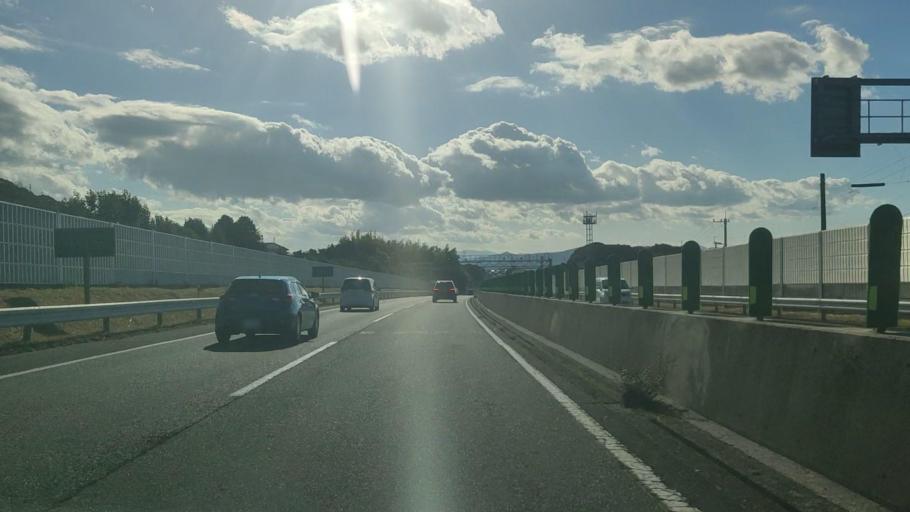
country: JP
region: Fukuoka
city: Nakama
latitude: 33.8258
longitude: 130.7634
